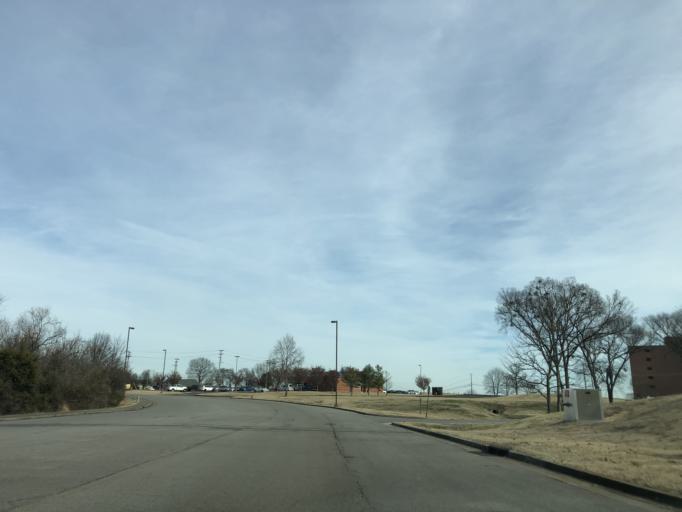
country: US
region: Tennessee
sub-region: Davidson County
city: Nashville
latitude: 36.2158
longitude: -86.7446
